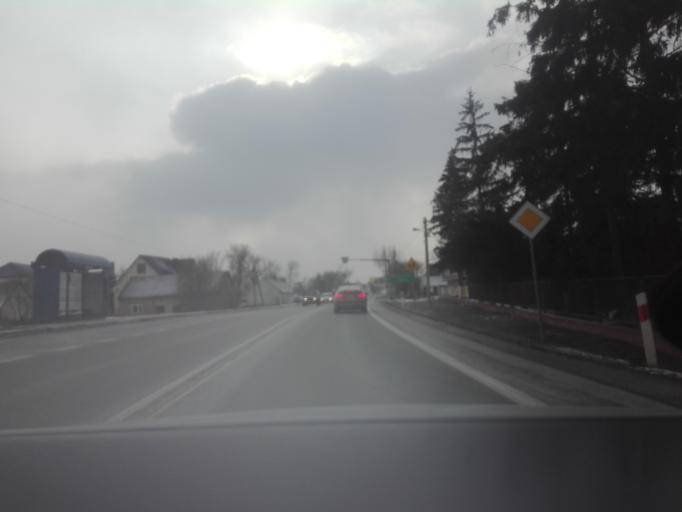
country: PL
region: Subcarpathian Voivodeship
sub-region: Powiat tarnobrzeski
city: Sokolniki
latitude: 50.6584
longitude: 21.7838
